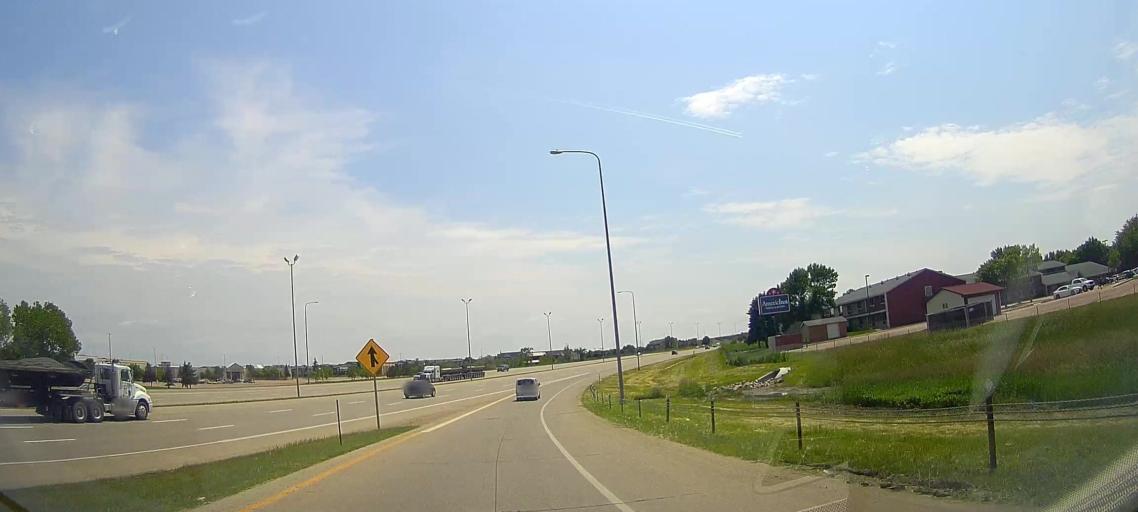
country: US
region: South Dakota
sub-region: Lincoln County
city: Tea
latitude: 43.5132
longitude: -96.7811
